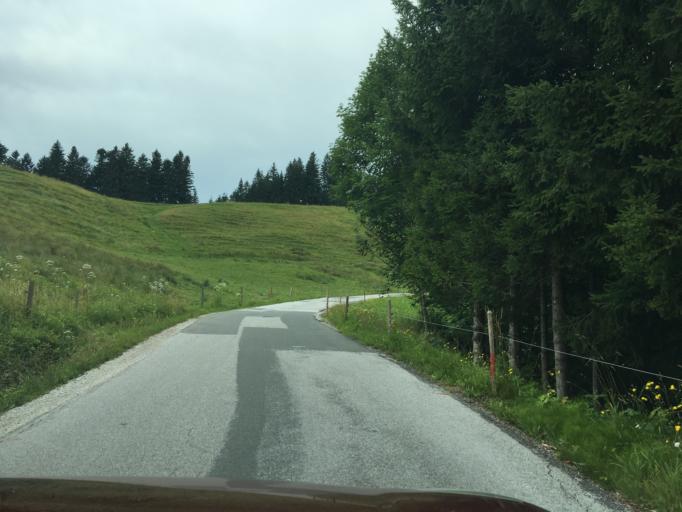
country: AT
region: Salzburg
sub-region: Politischer Bezirk Hallein
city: Abtenau
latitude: 47.5993
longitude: 13.3336
